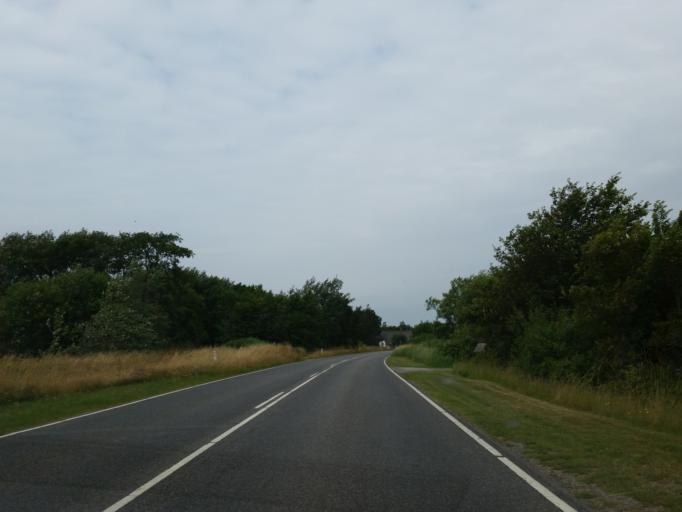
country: DE
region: Schleswig-Holstein
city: List
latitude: 55.1397
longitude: 8.5474
